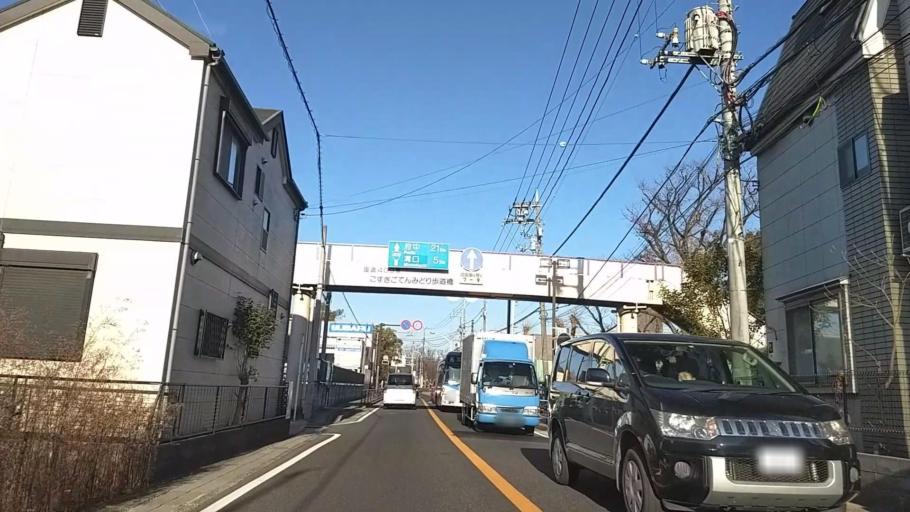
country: JP
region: Kanagawa
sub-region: Kawasaki-shi
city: Kawasaki
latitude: 35.5826
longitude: 139.6502
